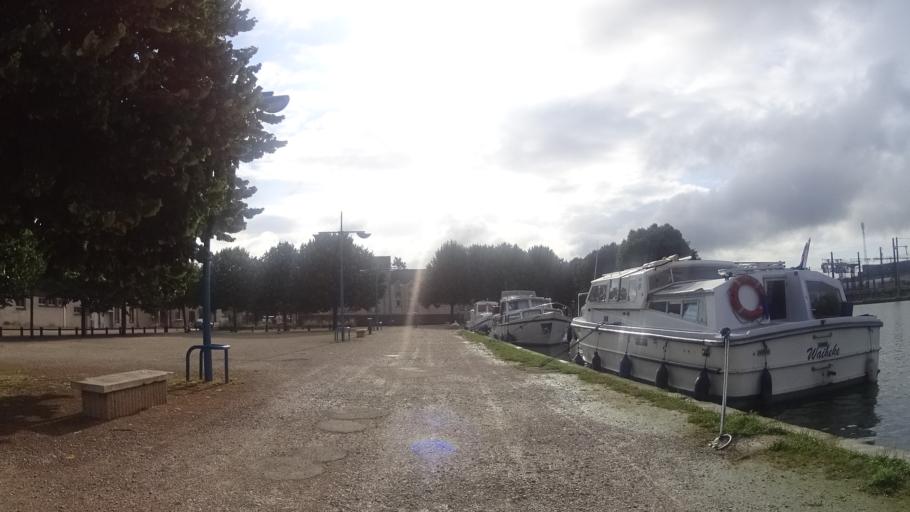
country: FR
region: Bourgogne
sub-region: Departement de l'Yonne
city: Migennes
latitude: 47.9617
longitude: 3.5087
